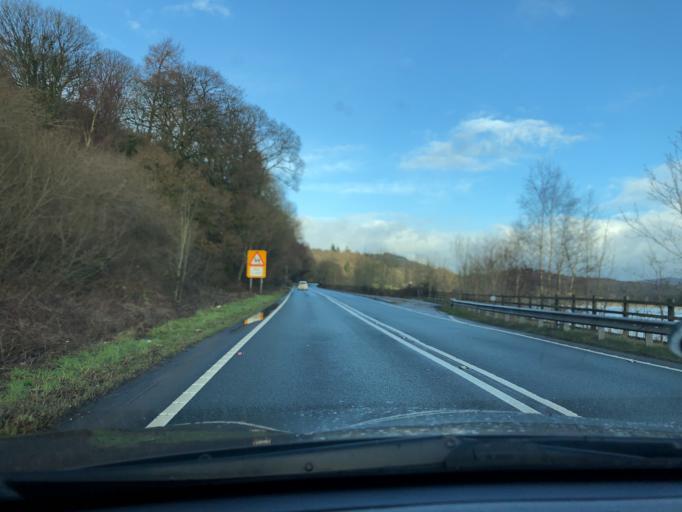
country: GB
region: England
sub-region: Cumbria
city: Ulverston
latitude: 54.2386
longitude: -3.0482
